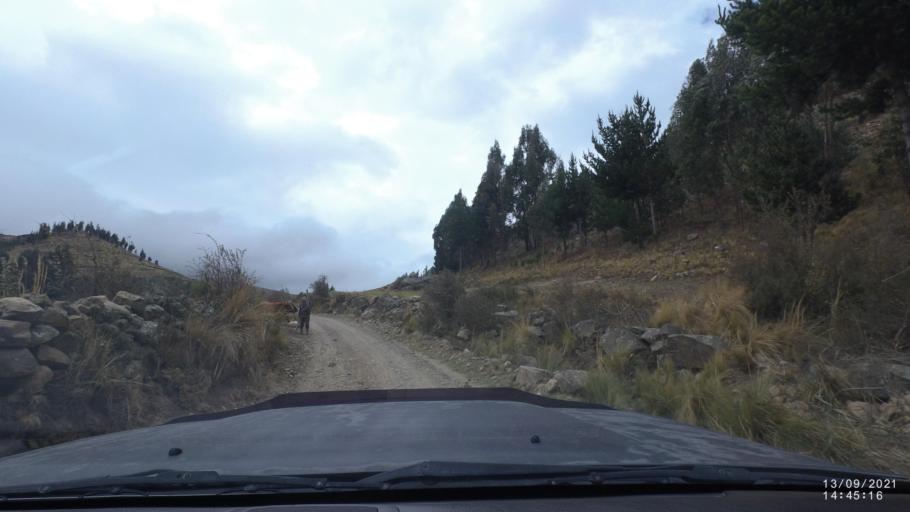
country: BO
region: Cochabamba
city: Colomi
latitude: -17.3541
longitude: -65.8093
